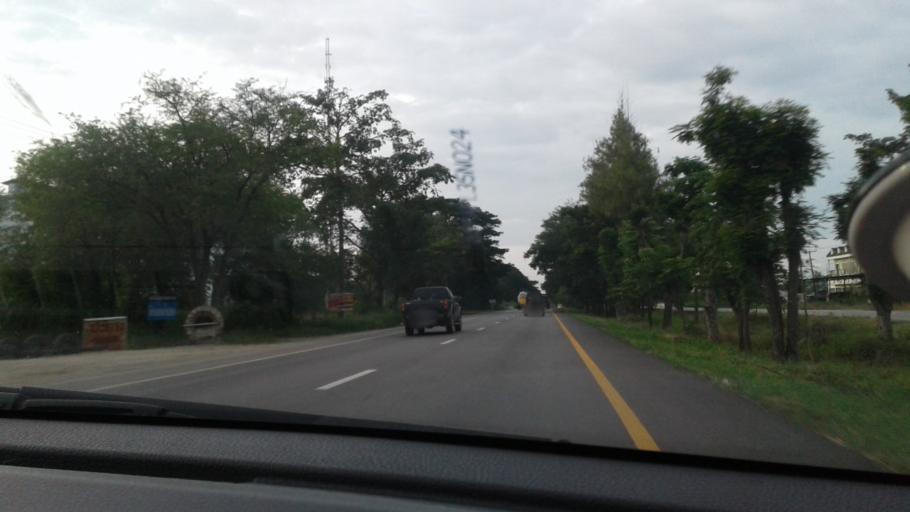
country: TH
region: Prachuap Khiri Khan
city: Pran Buri
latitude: 12.4369
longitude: 99.9118
